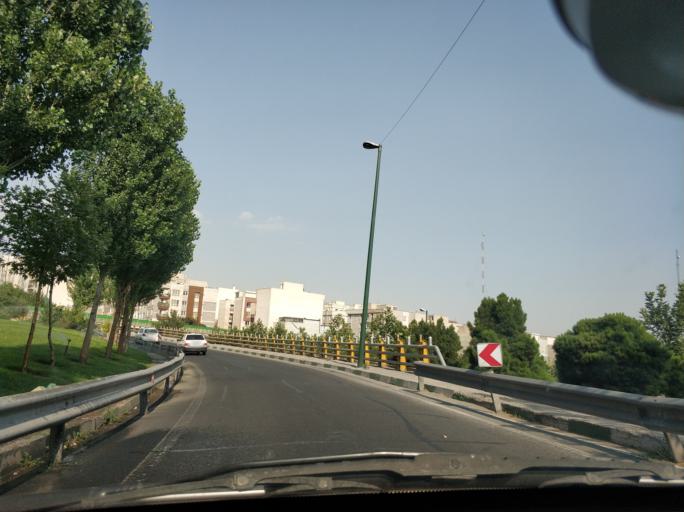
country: IR
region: Tehran
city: Tehran
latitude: 35.7393
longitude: 51.3688
